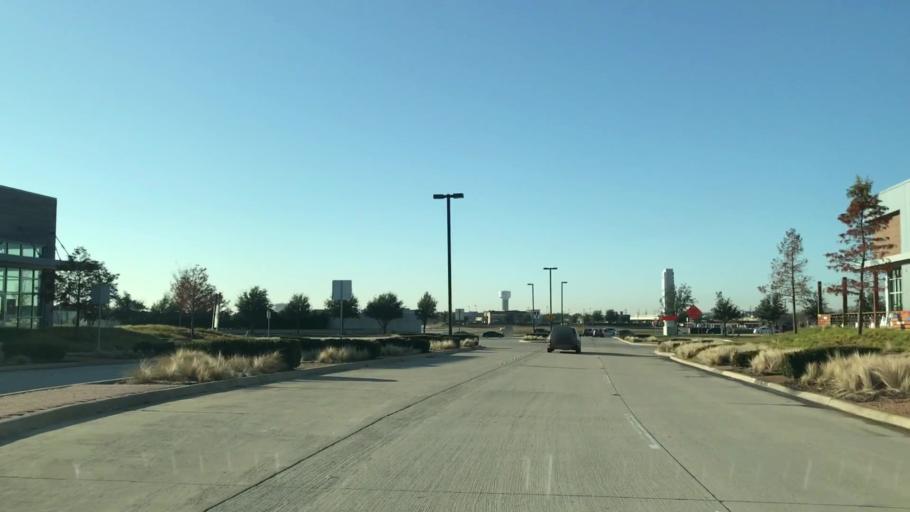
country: US
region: Texas
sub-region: Dallas County
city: Coppell
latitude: 32.9252
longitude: -96.9907
